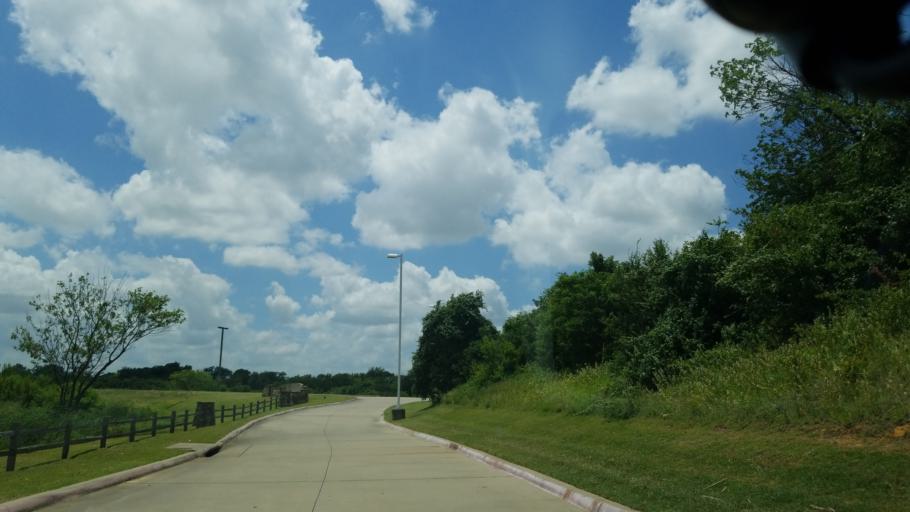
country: US
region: Texas
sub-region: Dallas County
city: Carrollton
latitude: 32.9632
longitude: -96.9394
